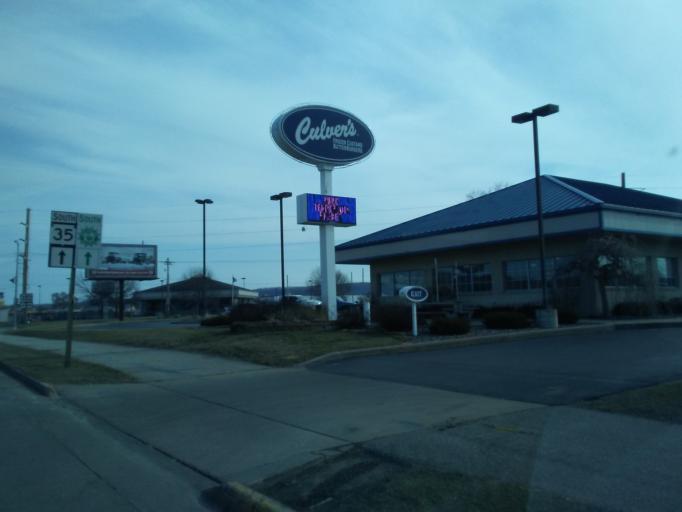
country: US
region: Wisconsin
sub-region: Crawford County
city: Prairie du Chien
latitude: 43.0291
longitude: -91.1289
